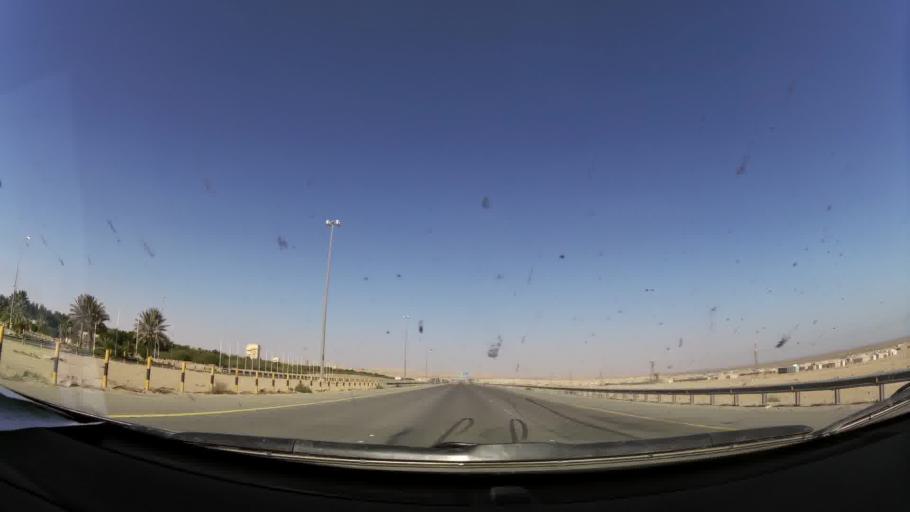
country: KW
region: Muhafazat al Jahra'
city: Al Jahra'
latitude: 29.4646
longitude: 47.7638
